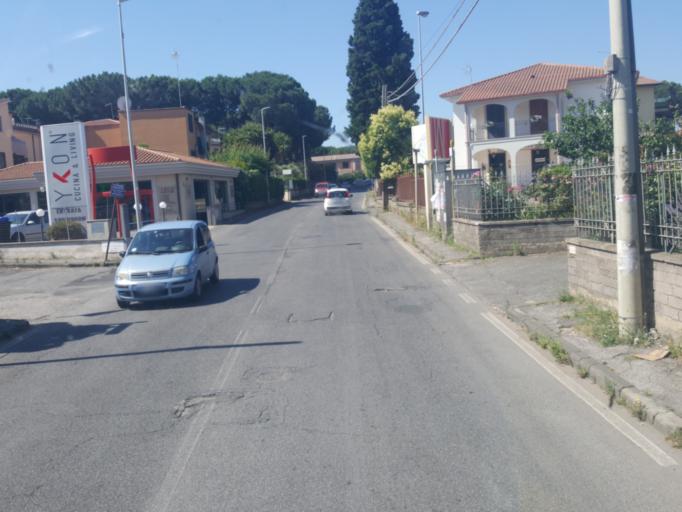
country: IT
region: Latium
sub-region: Citta metropolitana di Roma Capitale
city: Frascati
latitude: 41.8242
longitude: 12.6445
